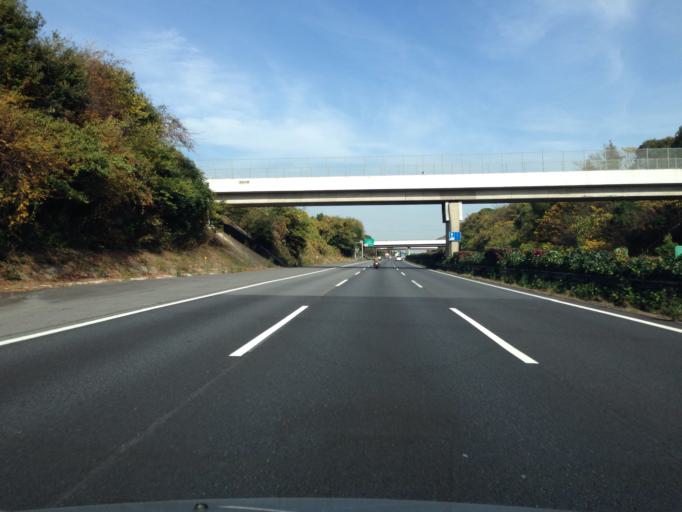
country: JP
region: Ibaraki
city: Naka
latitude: 36.1110
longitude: 140.1790
